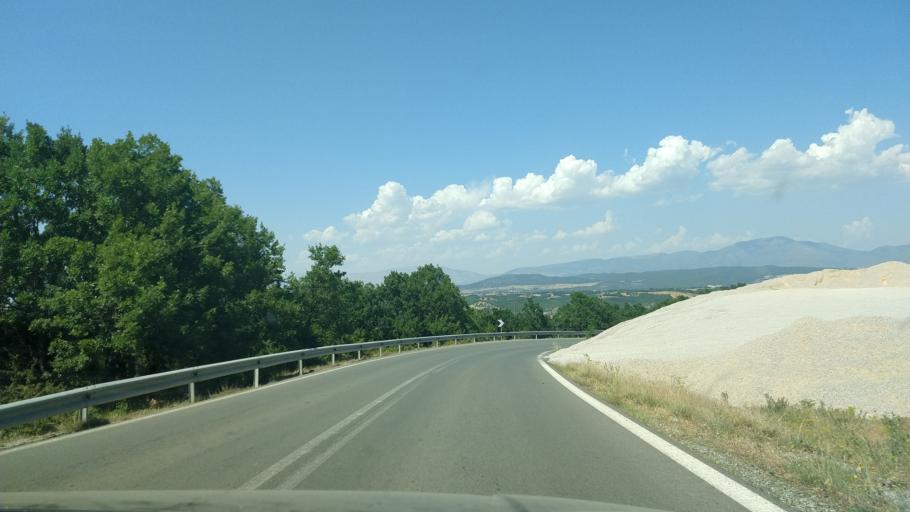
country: GR
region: West Macedonia
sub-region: Nomos Grevenon
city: Grevena
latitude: 40.0330
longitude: 21.4834
